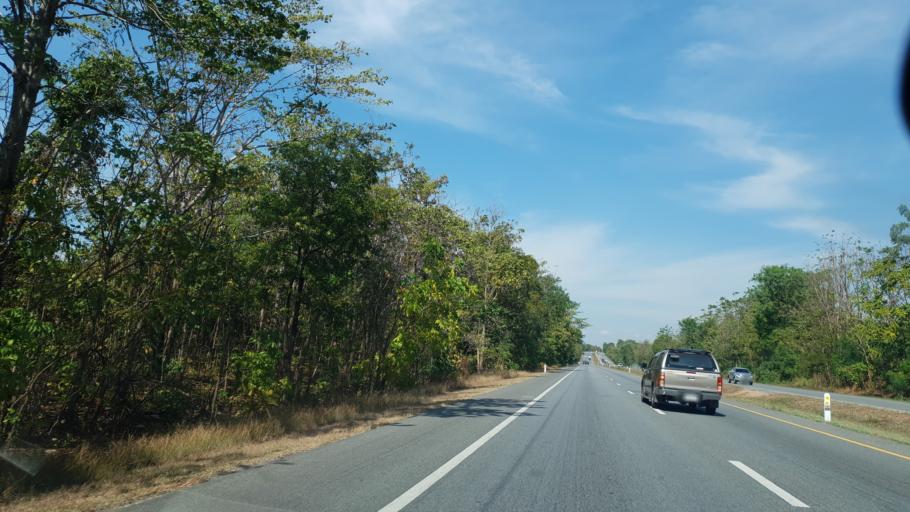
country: TH
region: Uttaradit
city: Thong Saen Khan
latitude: 17.4126
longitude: 100.2284
